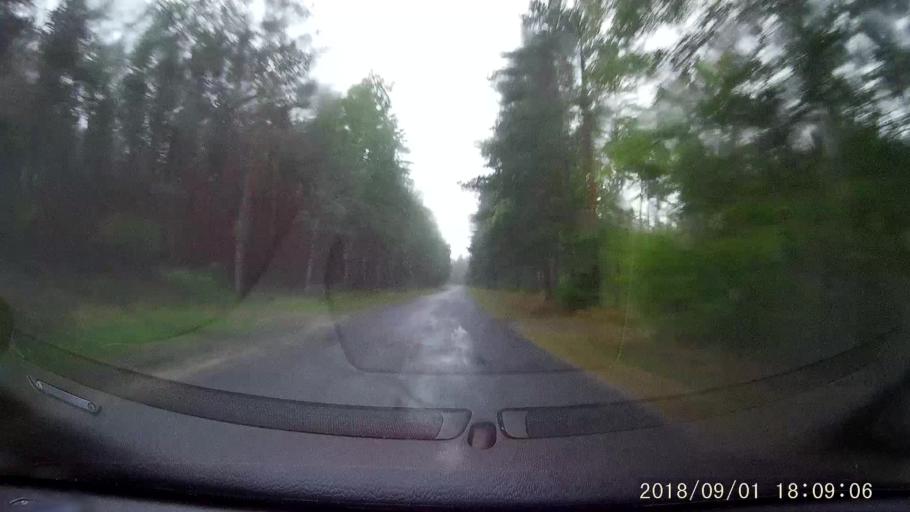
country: PL
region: Lubusz
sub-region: Powiat zaganski
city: Gozdnica
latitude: 51.3429
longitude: 15.1139
